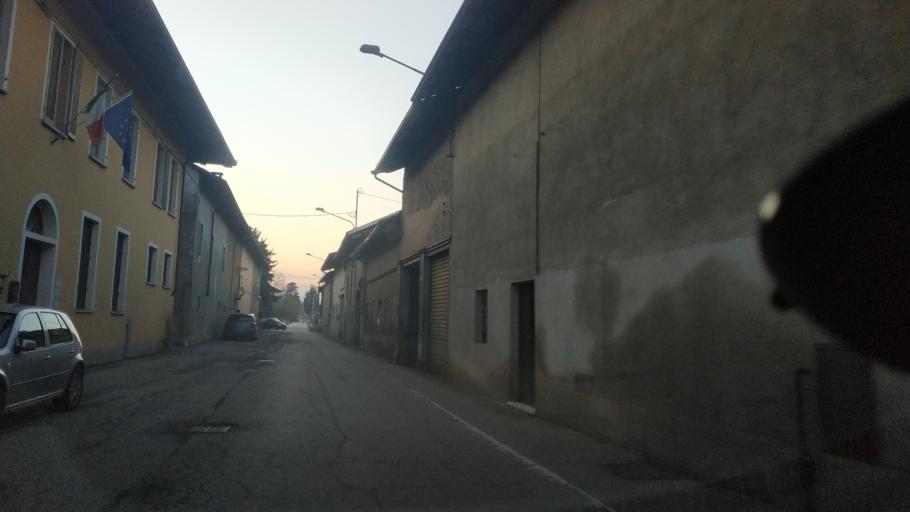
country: IT
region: Piedmont
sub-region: Provincia di Torino
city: Caluso
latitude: 45.2666
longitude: 7.8773
